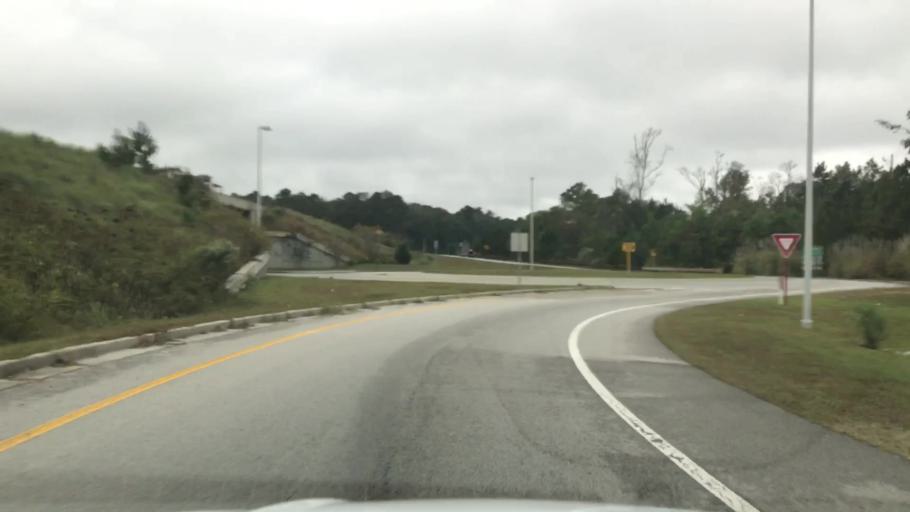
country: US
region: South Carolina
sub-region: Hampton County
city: Yemassee
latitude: 32.6024
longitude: -80.7590
